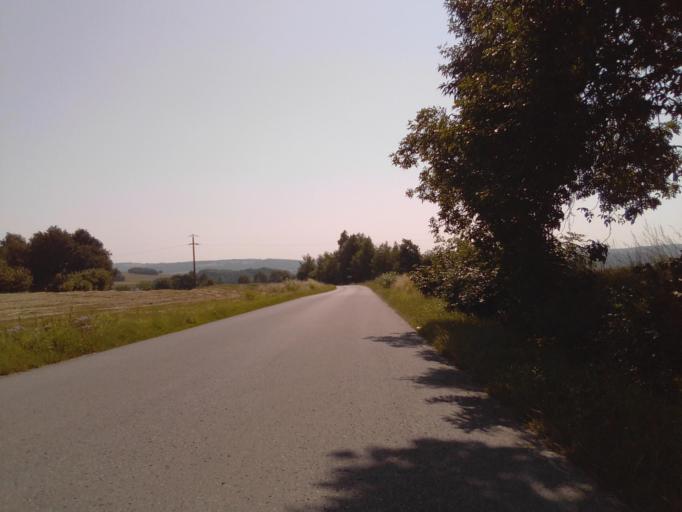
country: PL
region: Subcarpathian Voivodeship
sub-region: Powiat ropczycko-sedziszowski
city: Zagorzyce
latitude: 50.0106
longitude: 21.6293
